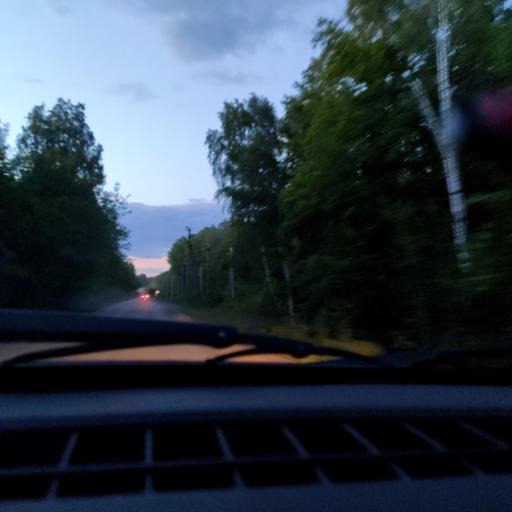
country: RU
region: Bashkortostan
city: Avdon
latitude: 54.6523
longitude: 55.5826
